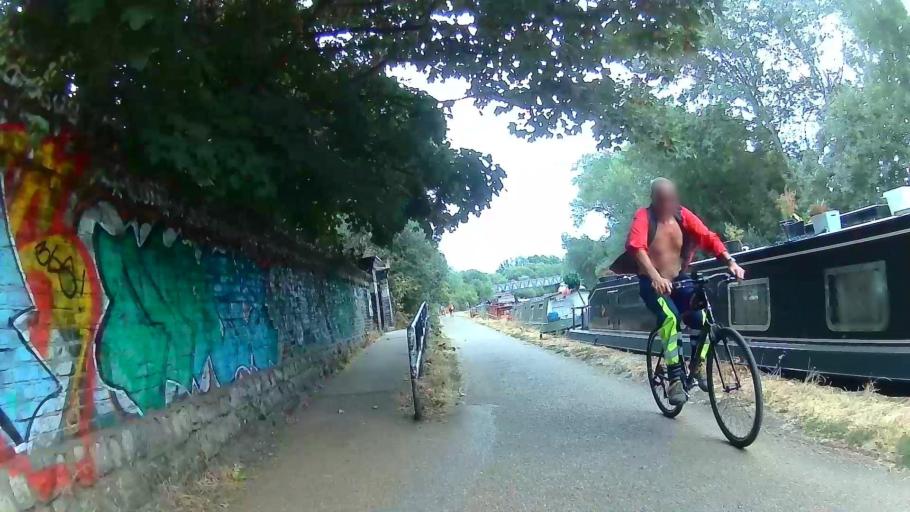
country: GB
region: England
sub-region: Greater London
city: Hackney
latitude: 51.5609
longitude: -0.0427
